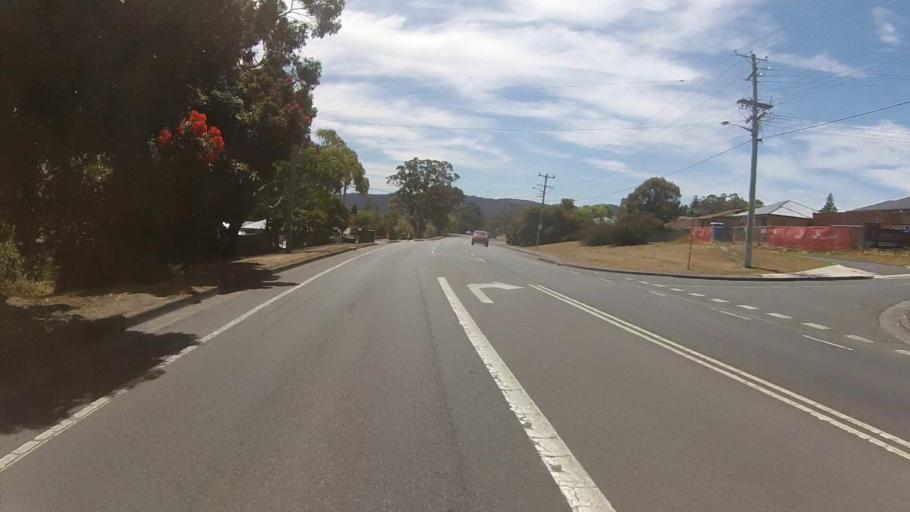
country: AU
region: Tasmania
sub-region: Kingborough
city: Kingston
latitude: -42.9807
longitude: 147.2982
